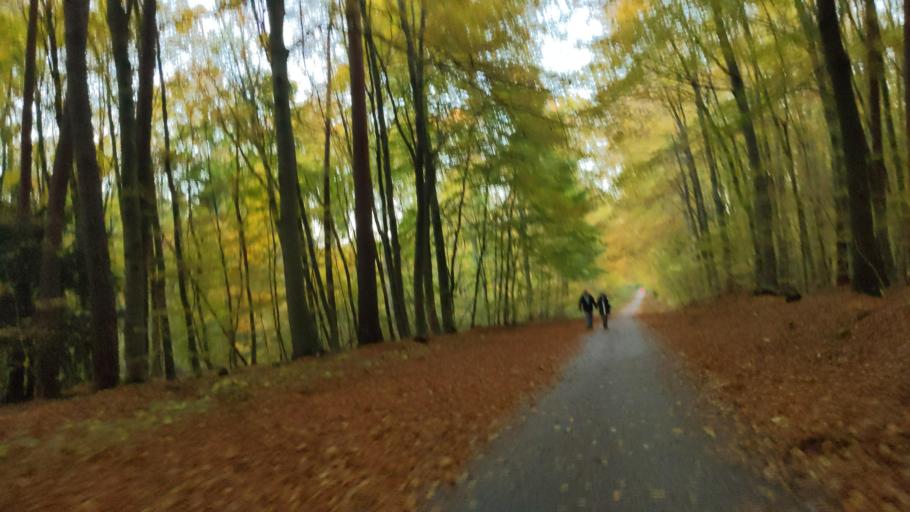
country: DE
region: Schleswig-Holstein
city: Bad Schwartau
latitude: 53.8897
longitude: 10.7515
